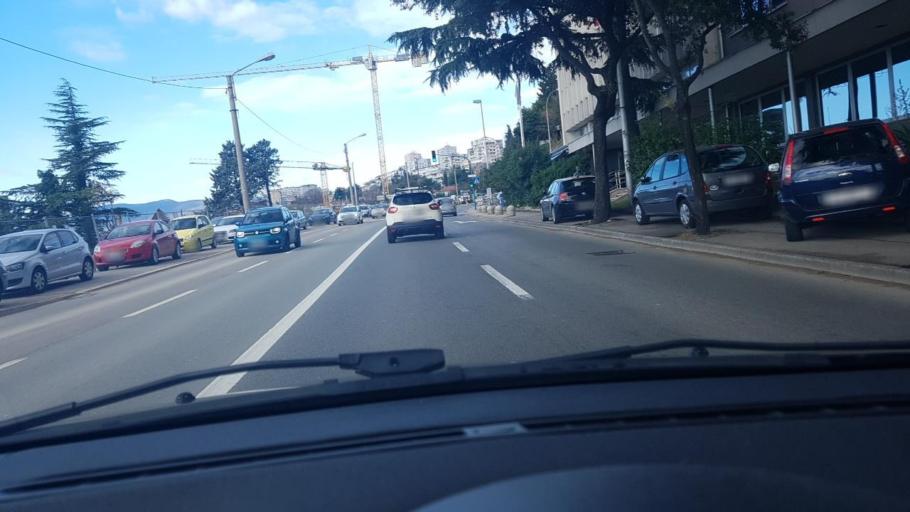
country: HR
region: Primorsko-Goranska
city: Rijeka
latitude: 45.3360
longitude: 14.4167
